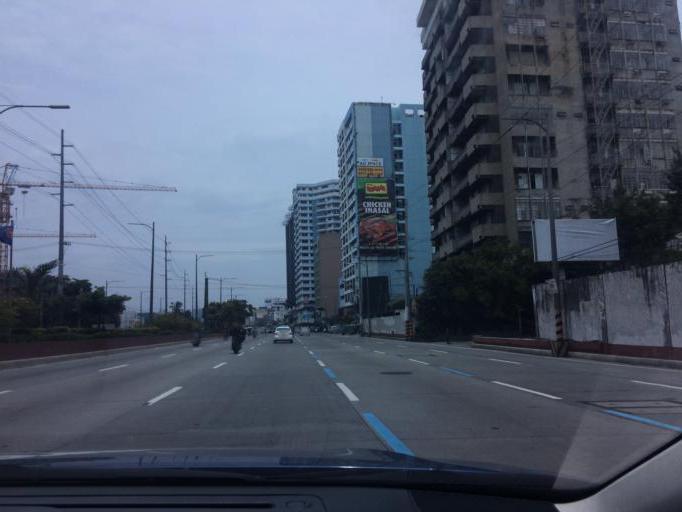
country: PH
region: Metro Manila
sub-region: Makati City
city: Makati City
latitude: 14.5252
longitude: 120.9938
